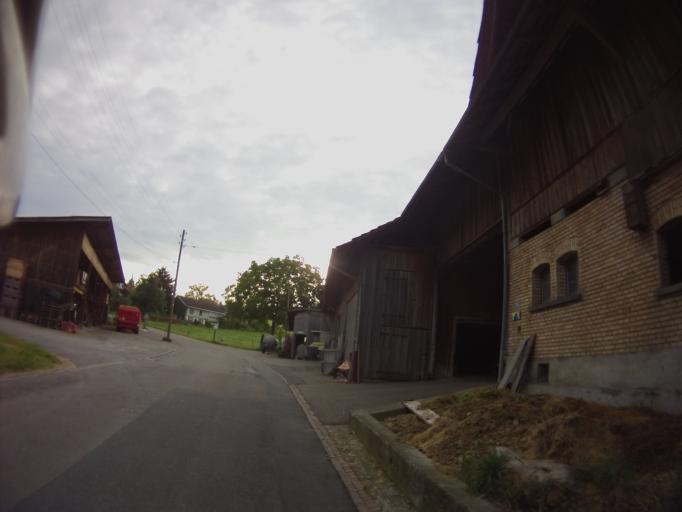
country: CH
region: Zurich
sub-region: Bezirk Affoltern
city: Knonau
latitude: 47.2267
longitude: 8.4859
